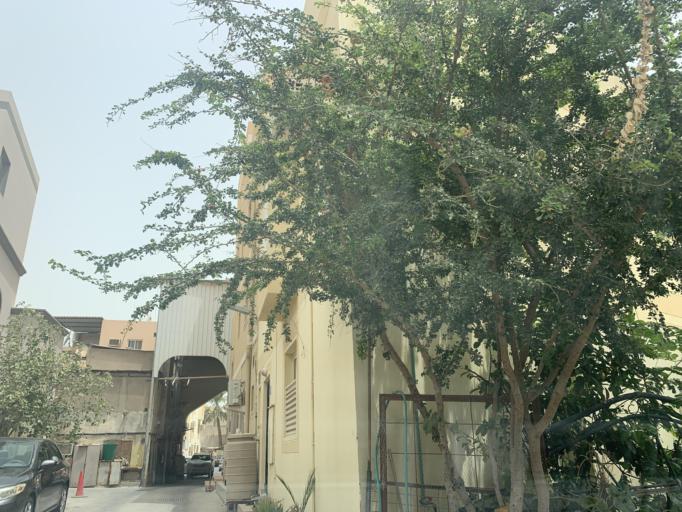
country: BH
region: Manama
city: Jidd Hafs
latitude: 26.2299
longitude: 50.5280
